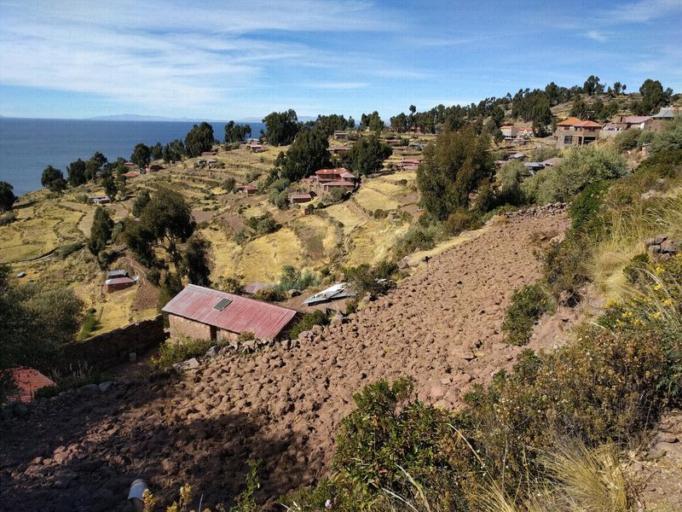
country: PE
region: Puno
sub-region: Provincia de Puno
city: Taquile
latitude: -15.7633
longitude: -69.6838
